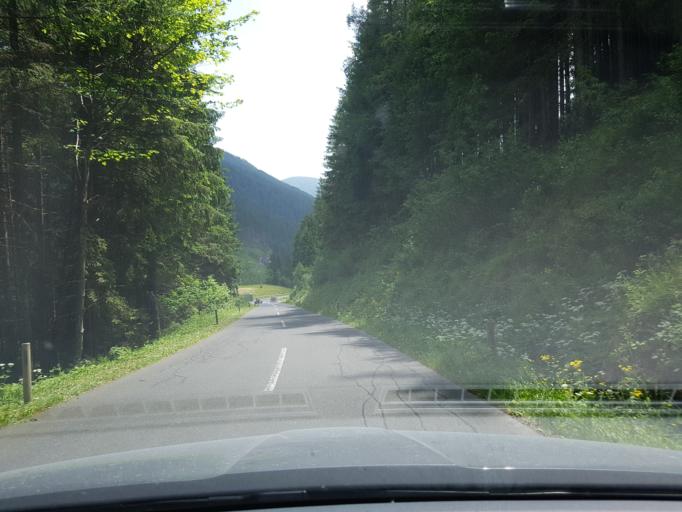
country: AT
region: Carinthia
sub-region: Politischer Bezirk Spittal an der Drau
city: Kleinkirchheim
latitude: 46.8690
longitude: 13.8829
